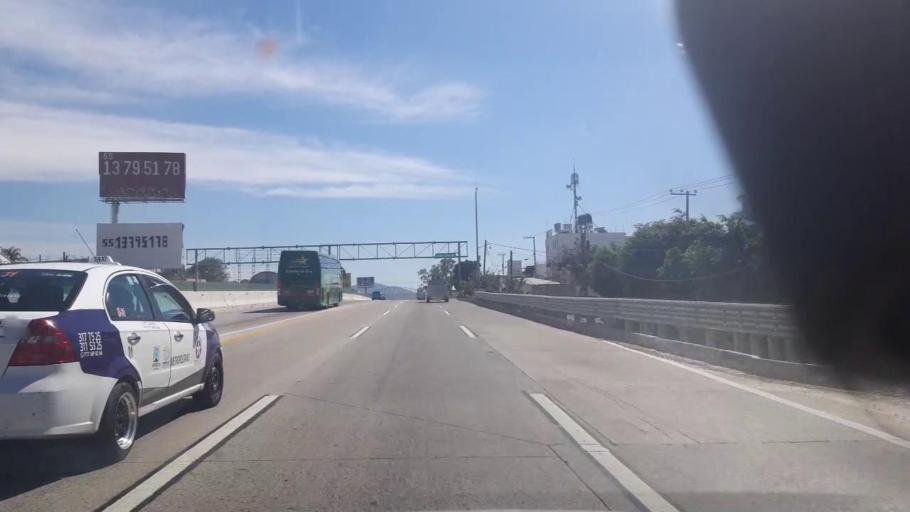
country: MX
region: Morelos
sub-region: Cuernavaca
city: Colonia los Cerritos
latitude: 18.9566
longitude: -99.2026
